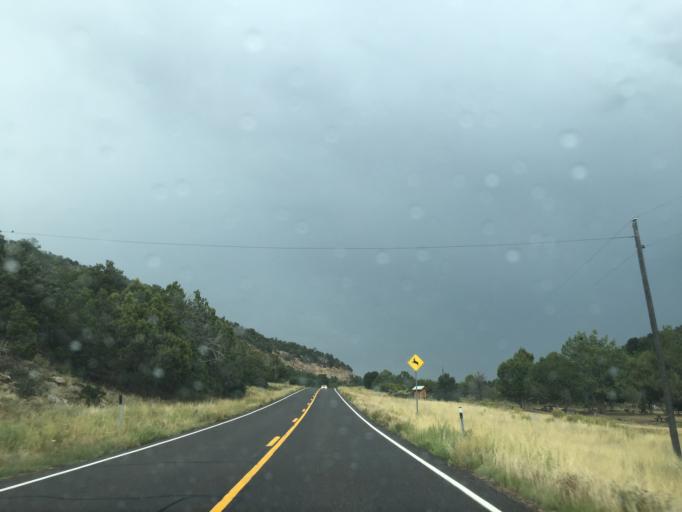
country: US
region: Utah
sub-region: Washington County
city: Hildale
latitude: 37.2374
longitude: -112.8531
